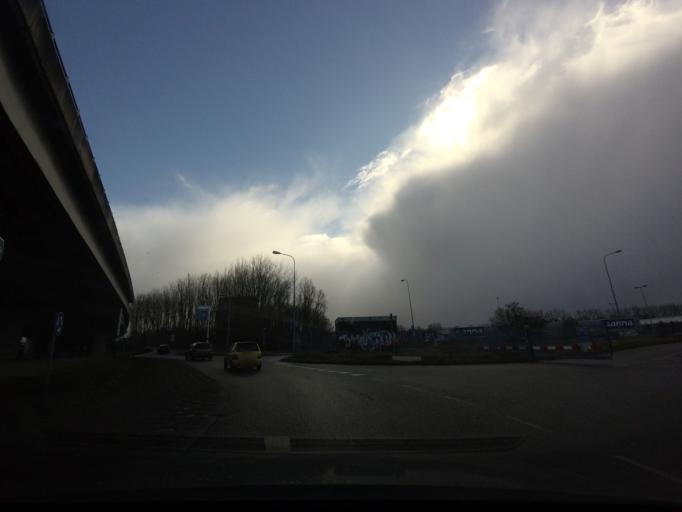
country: NL
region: Groningen
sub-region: Gemeente Groningen
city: Groningen
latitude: 53.2113
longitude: 6.5437
